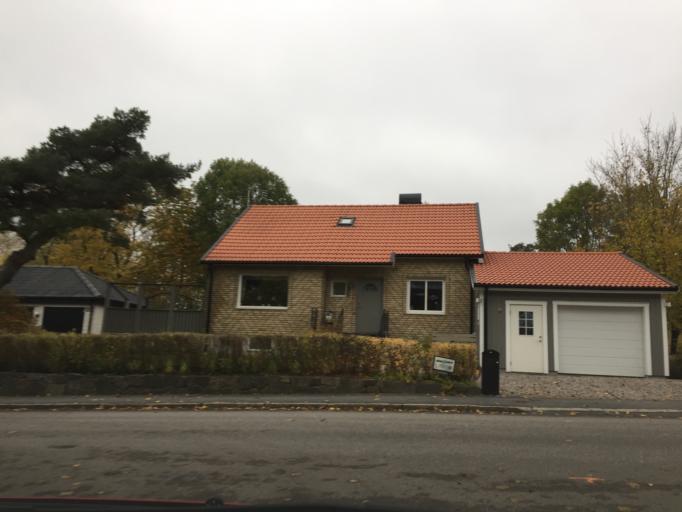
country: SE
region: Vaestra Goetaland
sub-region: Trollhattan
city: Trollhattan
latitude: 58.2685
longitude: 12.2771
